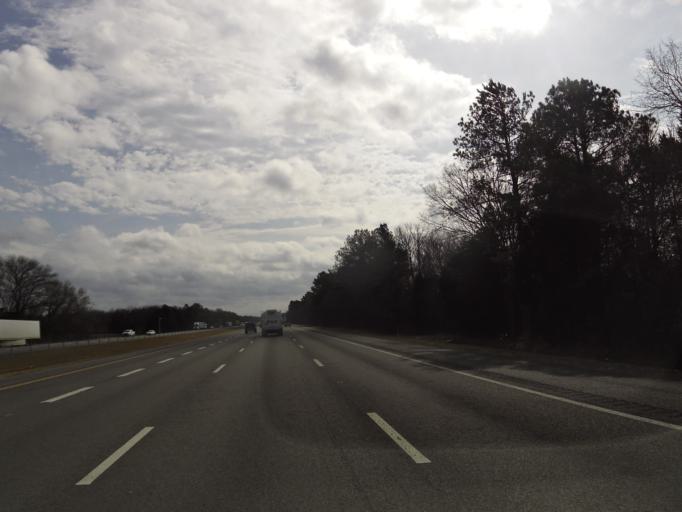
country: US
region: Tennessee
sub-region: Rutherford County
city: Smyrna
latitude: 35.9152
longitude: -86.5105
